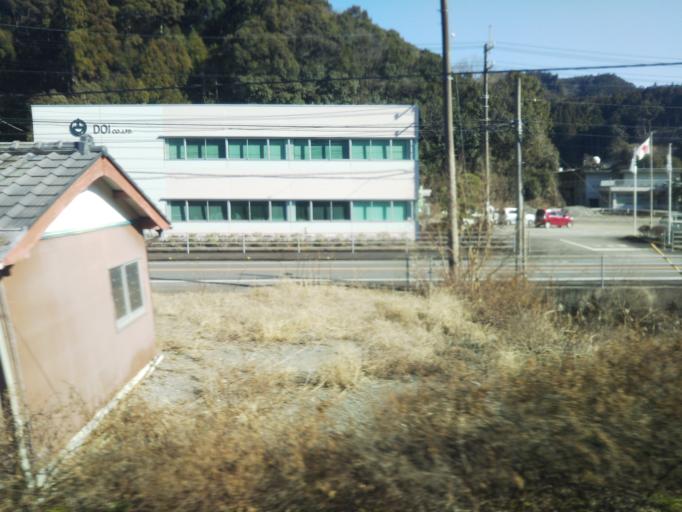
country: JP
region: Kochi
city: Nakamura
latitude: 33.1059
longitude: 133.0987
